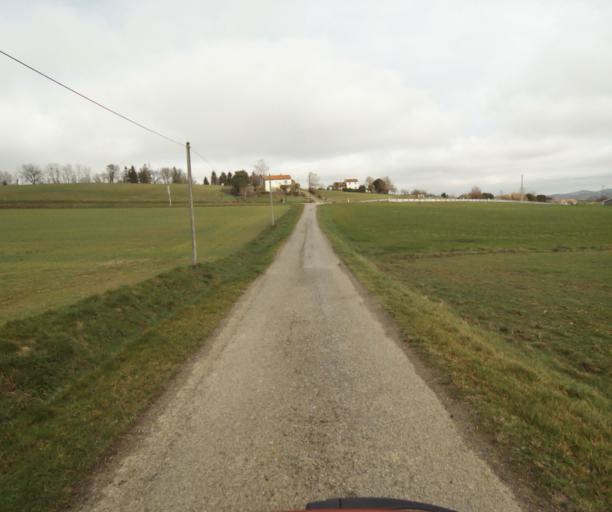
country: FR
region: Midi-Pyrenees
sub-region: Departement de l'Ariege
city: Pamiers
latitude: 43.1094
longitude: 1.5202
